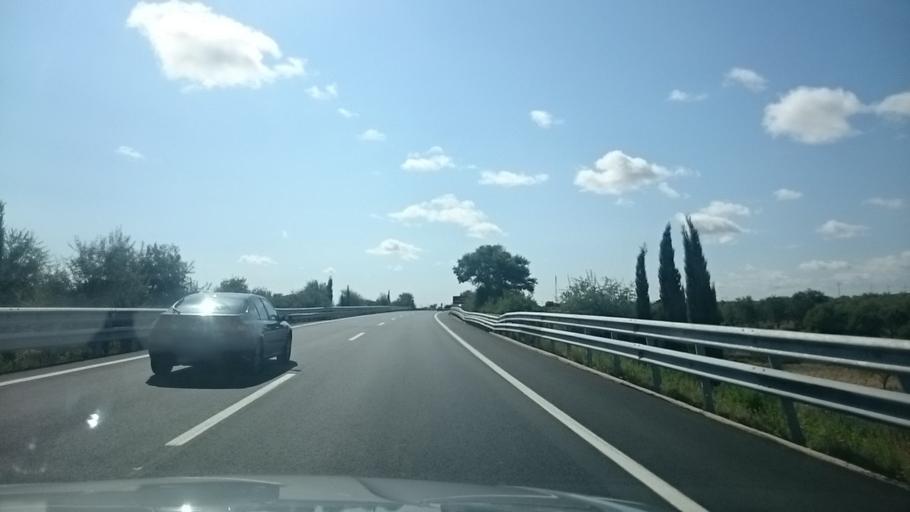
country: ES
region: Navarre
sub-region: Provincia de Navarra
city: Corella
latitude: 42.1217
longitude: -1.7446
